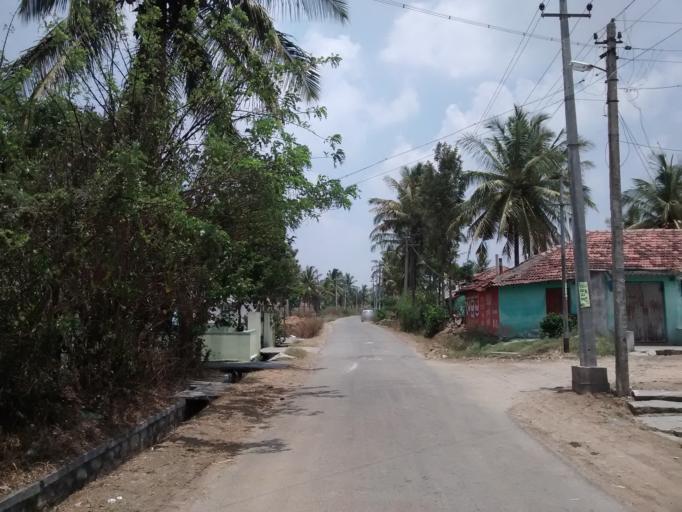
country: IN
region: Karnataka
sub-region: Hassan
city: Hassan
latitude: 12.9478
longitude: 76.1564
